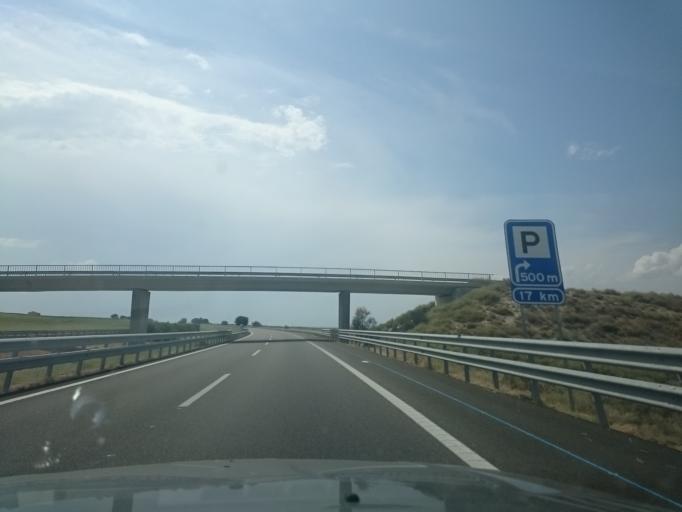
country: ES
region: Aragon
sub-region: Provincia de Huesca
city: Penalba
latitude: 41.5182
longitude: -0.0858
